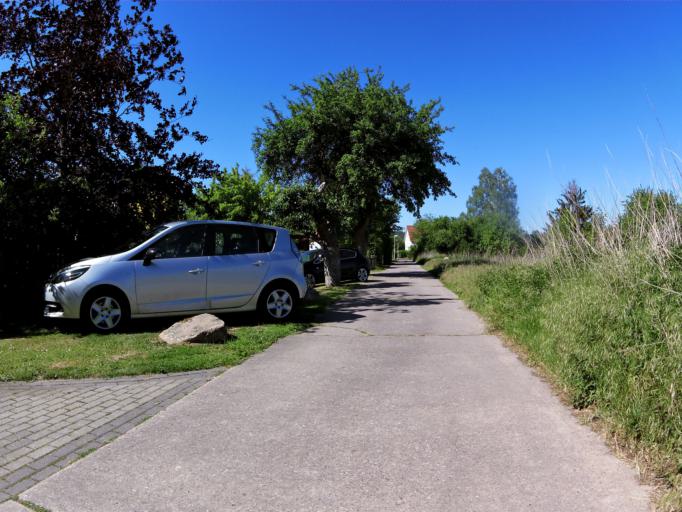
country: DE
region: Thuringia
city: Dippach
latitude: 50.9461
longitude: 10.0436
